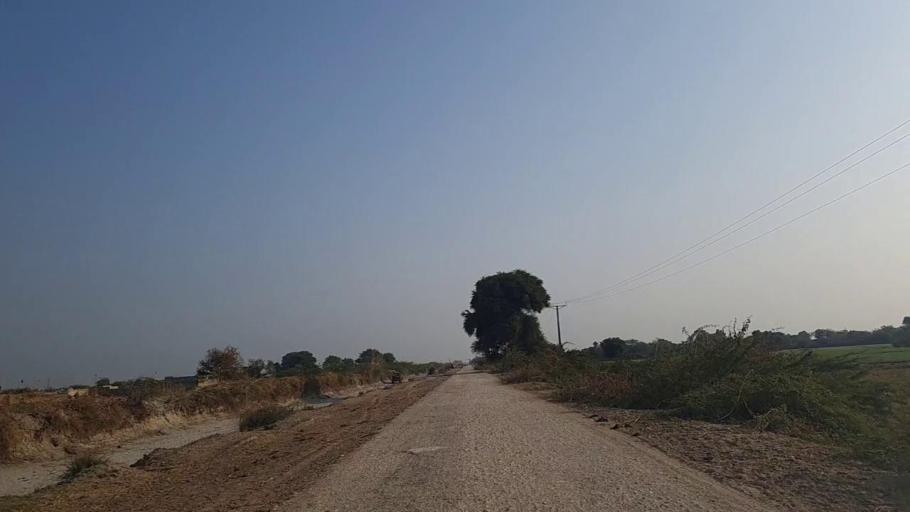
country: PK
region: Sindh
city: Jam Sahib
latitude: 26.2398
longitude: 68.5895
